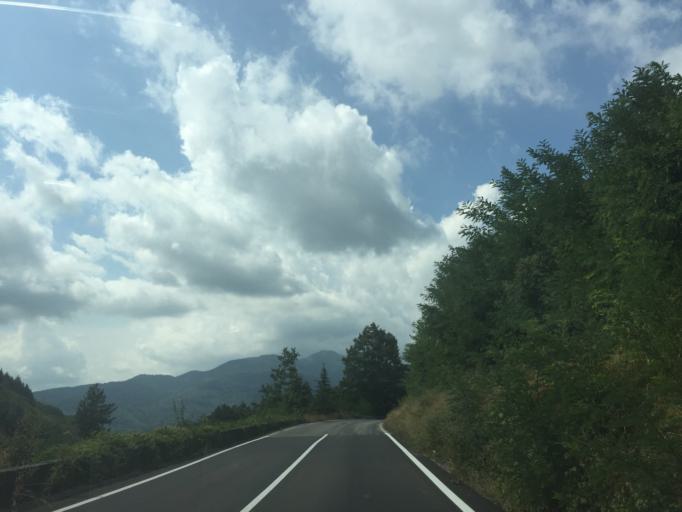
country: IT
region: Tuscany
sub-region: Provincia di Pistoia
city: San Marcello Pistoiese
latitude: 44.0502
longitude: 10.8063
